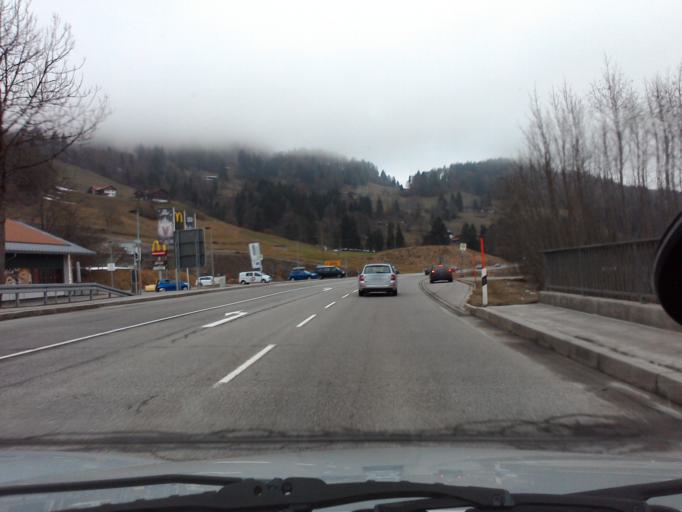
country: DE
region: Bavaria
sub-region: Swabia
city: Oberstdorf
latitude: 47.4256
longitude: 10.2671
